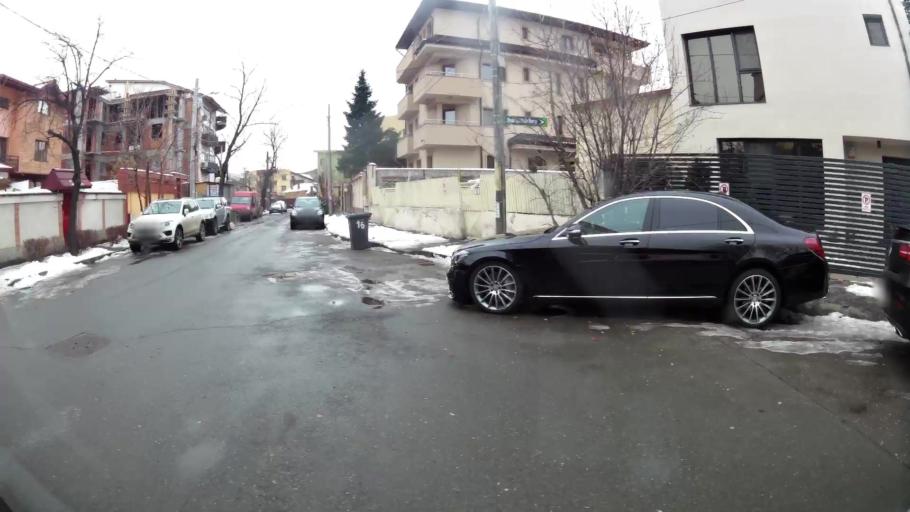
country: RO
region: Bucuresti
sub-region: Municipiul Bucuresti
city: Bucuresti
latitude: 44.4217
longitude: 26.0565
